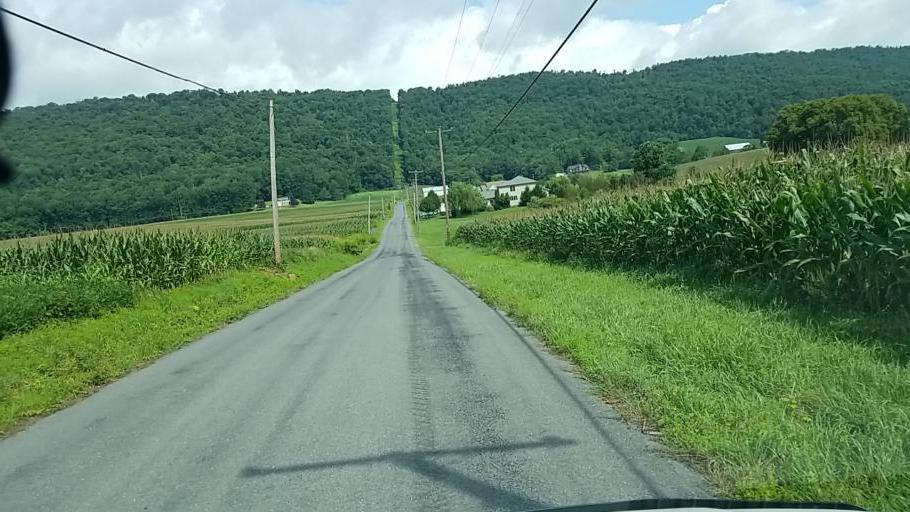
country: US
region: Pennsylvania
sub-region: Dauphin County
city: Millersburg
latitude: 40.5751
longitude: -76.9315
